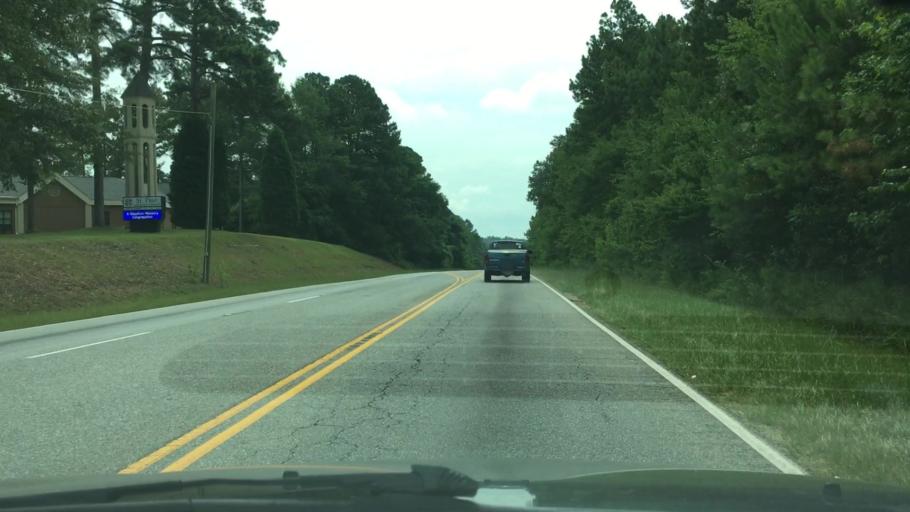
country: US
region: South Carolina
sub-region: Aiken County
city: Aiken
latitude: 33.5292
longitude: -81.7524
